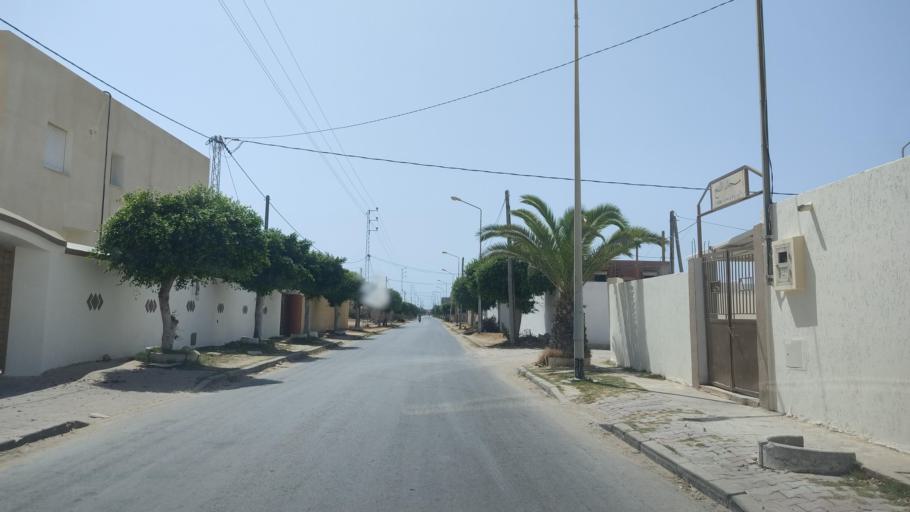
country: TN
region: Safaqis
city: Sfax
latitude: 34.6749
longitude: 10.7007
